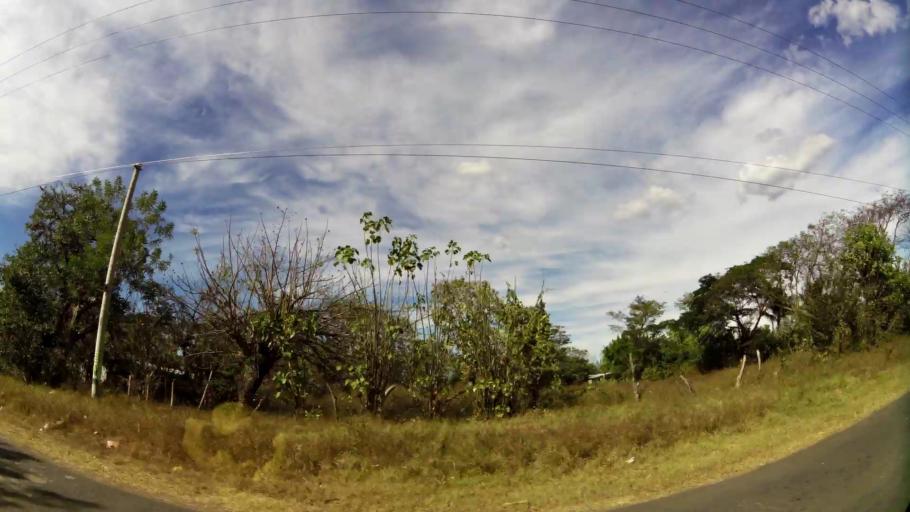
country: SV
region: San Salvador
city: Aguilares
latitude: 13.9615
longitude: -89.1304
